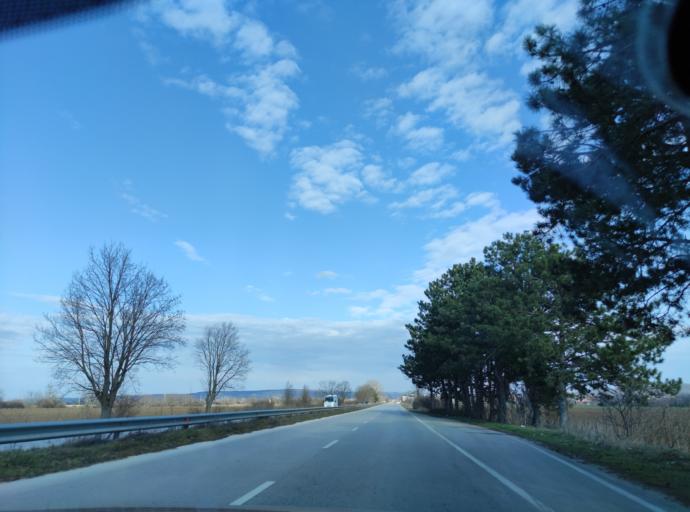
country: BG
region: Pleven
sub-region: Obshtina Dolna Mitropoliya
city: Dolna Mitropoliya
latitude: 43.4273
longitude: 24.5092
